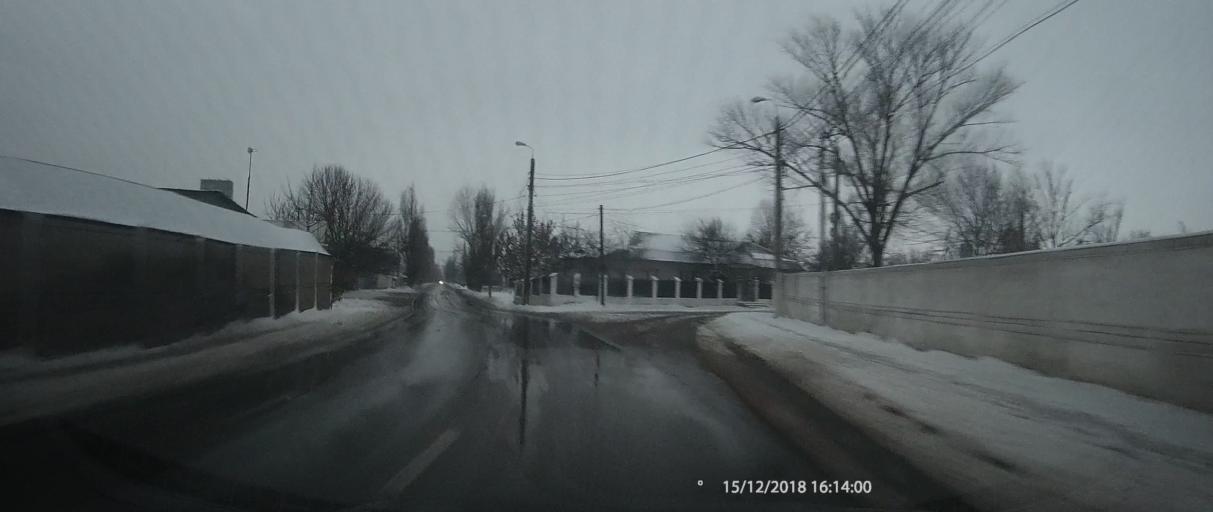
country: RO
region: Galati
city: Galati
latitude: 45.4614
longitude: 28.0320
